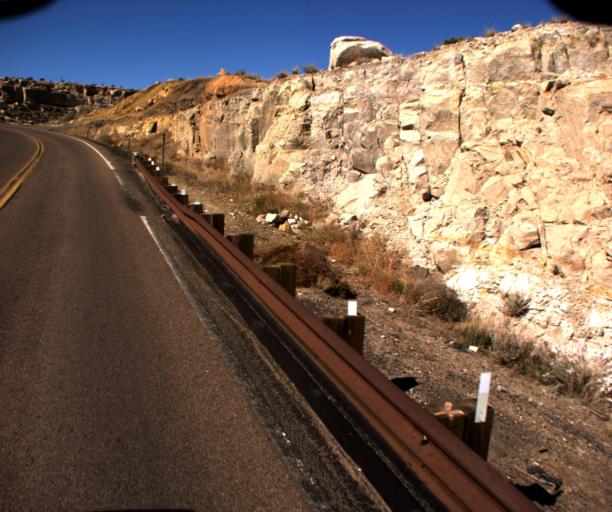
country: US
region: Arizona
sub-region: Navajo County
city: First Mesa
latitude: 35.8096
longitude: -110.5239
